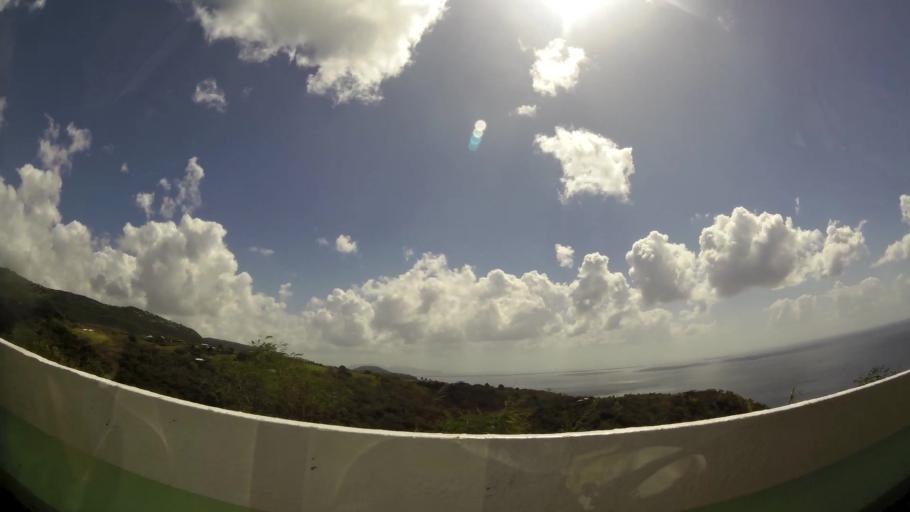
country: MQ
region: Martinique
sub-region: Martinique
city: Saint-Pierre
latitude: 14.6927
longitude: -61.1727
